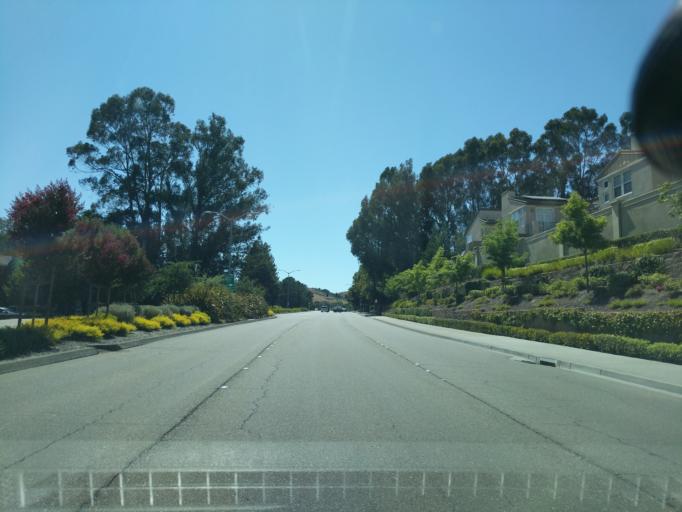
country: US
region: California
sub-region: Contra Costa County
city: San Ramon
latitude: 37.7738
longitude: -121.9862
